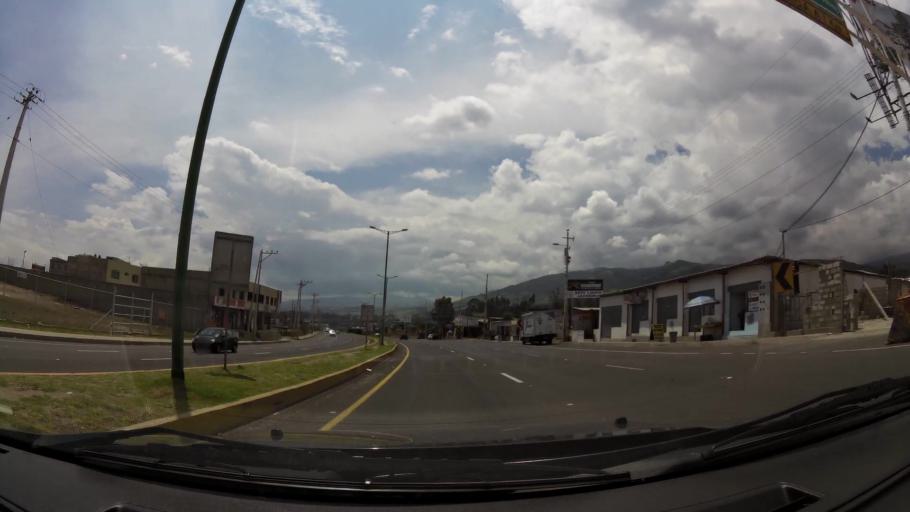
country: EC
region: Pichincha
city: Sangolqui
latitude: -0.2227
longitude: -78.3401
